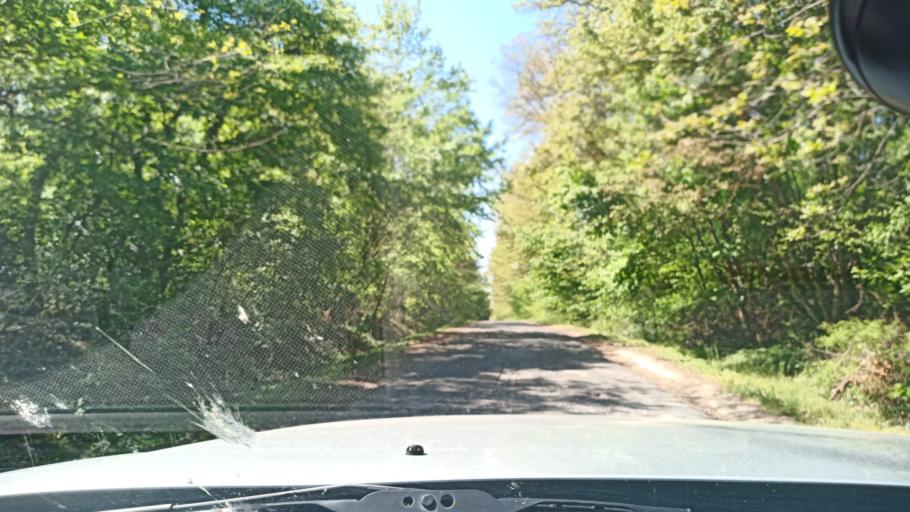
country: HU
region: Zala
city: Heviz
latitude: 46.7646
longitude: 17.1616
